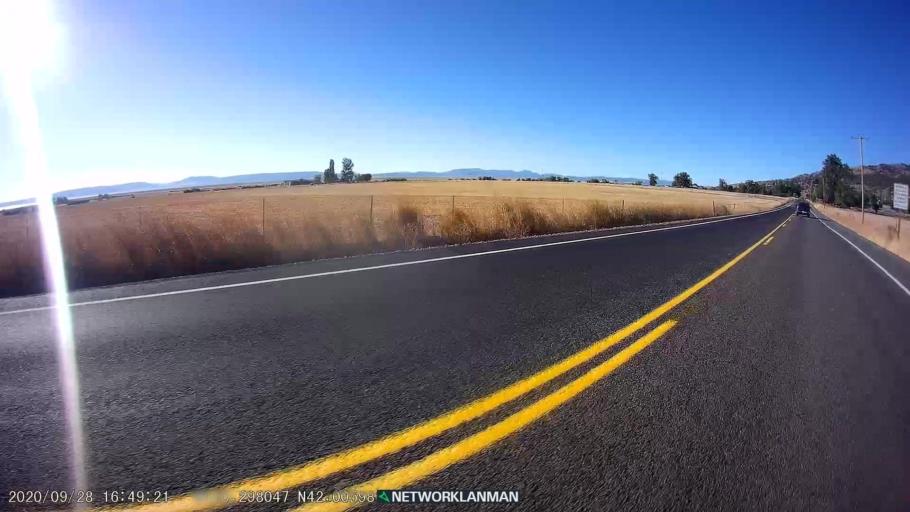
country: US
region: Oregon
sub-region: Lake County
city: Lakeview
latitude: 42.0063
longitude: -120.2980
